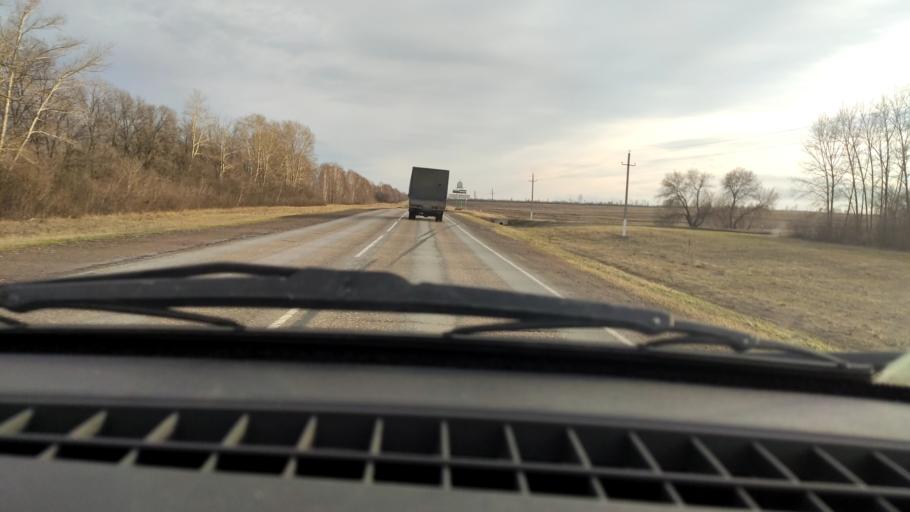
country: RU
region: Bashkortostan
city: Davlekanovo
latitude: 54.3423
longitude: 55.1734
